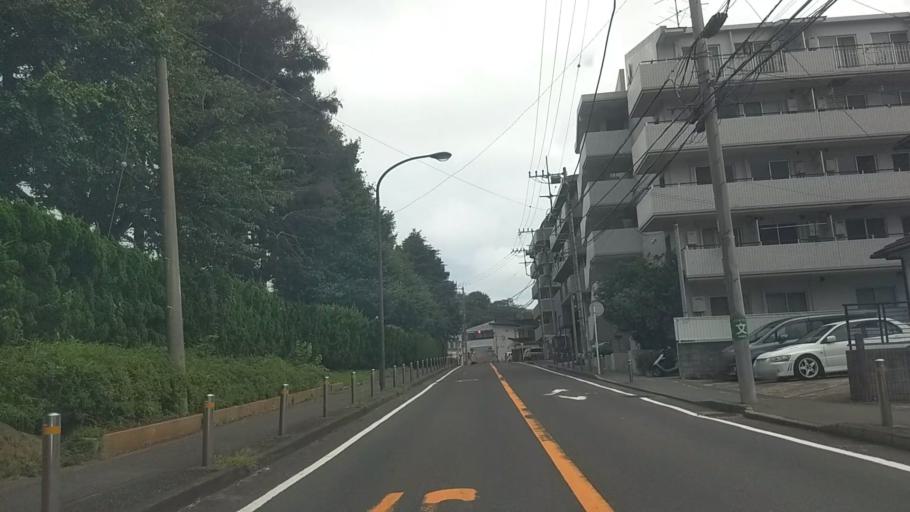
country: JP
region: Kanagawa
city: Yokosuka
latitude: 35.2715
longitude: 139.6609
